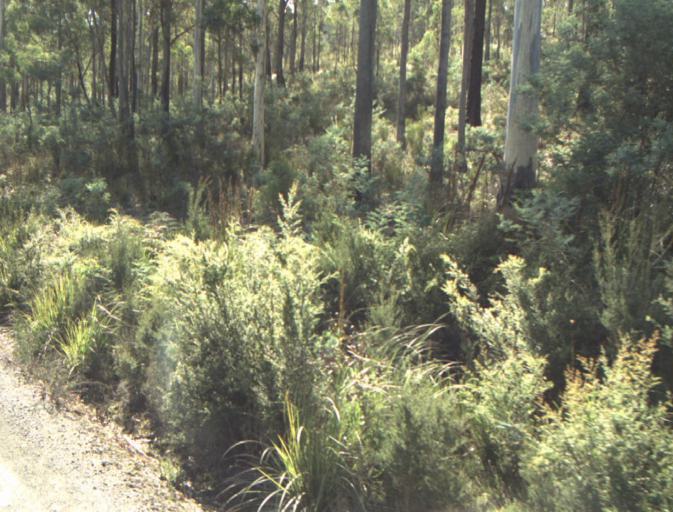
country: AU
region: Tasmania
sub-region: Launceston
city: Mayfield
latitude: -41.2739
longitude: 147.1051
